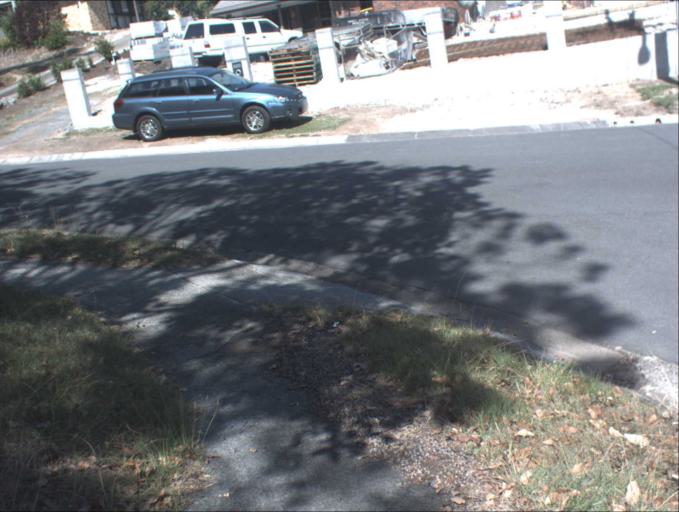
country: AU
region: Queensland
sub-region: Logan
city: Slacks Creek
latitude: -27.6571
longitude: 153.1806
